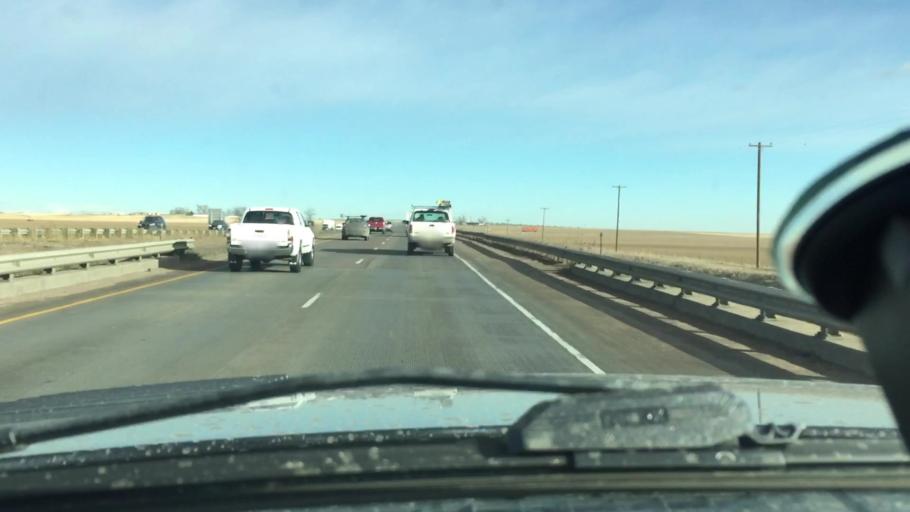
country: US
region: Colorado
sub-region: Weld County
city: Johnstown
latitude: 40.3210
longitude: -104.9798
